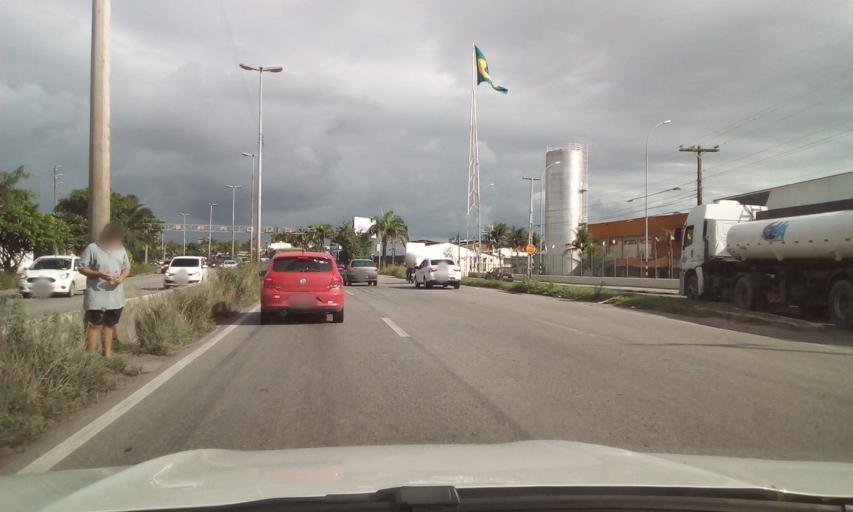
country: BR
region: Pernambuco
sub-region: Recife
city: Recife
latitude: -8.0290
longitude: -34.9431
